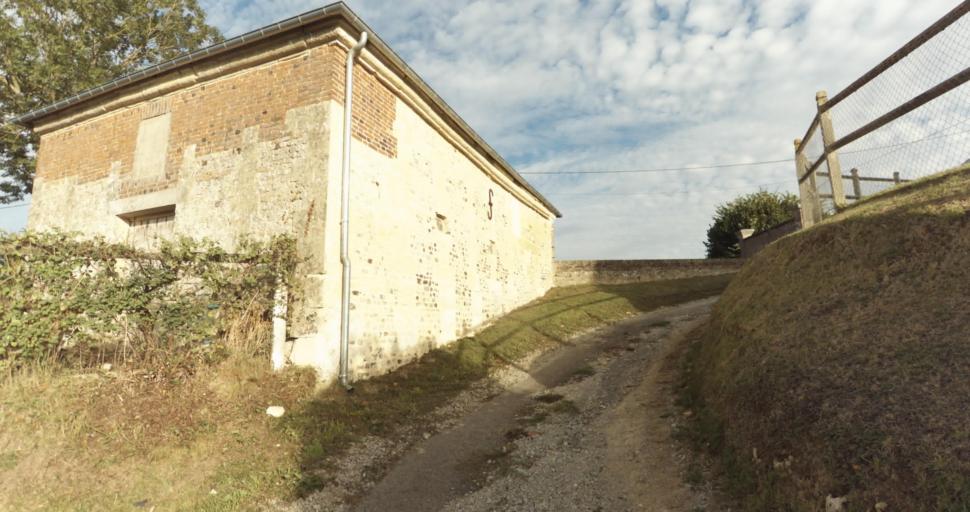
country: FR
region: Lower Normandy
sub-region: Departement de l'Orne
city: Vimoutiers
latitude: 48.8792
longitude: 0.2343
